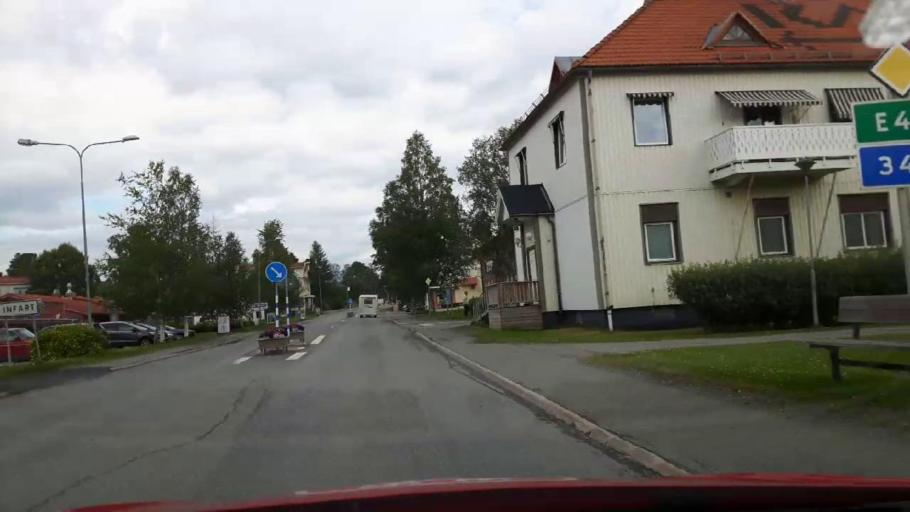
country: SE
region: Jaemtland
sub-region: Stroemsunds Kommun
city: Stroemsund
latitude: 63.5823
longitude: 15.3519
